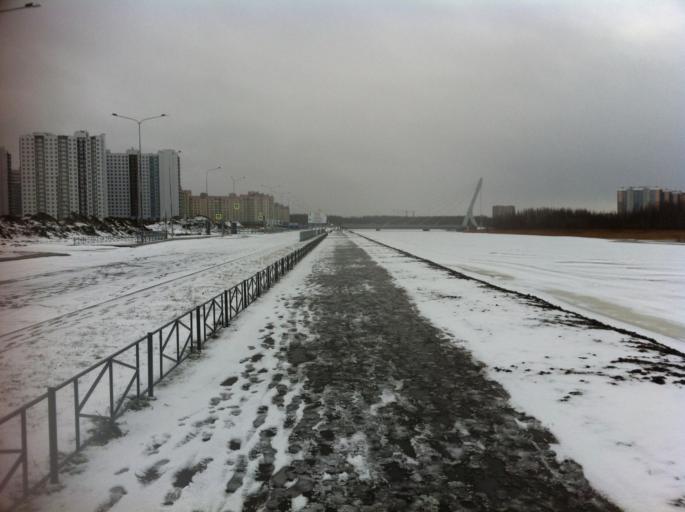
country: RU
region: St.-Petersburg
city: Sosnovaya Polyana
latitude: 59.8643
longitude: 30.1501
